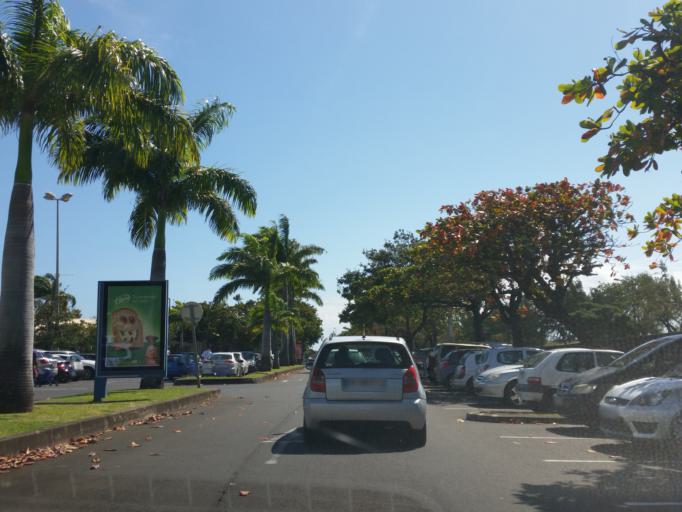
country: RE
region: Reunion
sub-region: Reunion
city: Sainte-Marie
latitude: -20.8924
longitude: 55.5013
